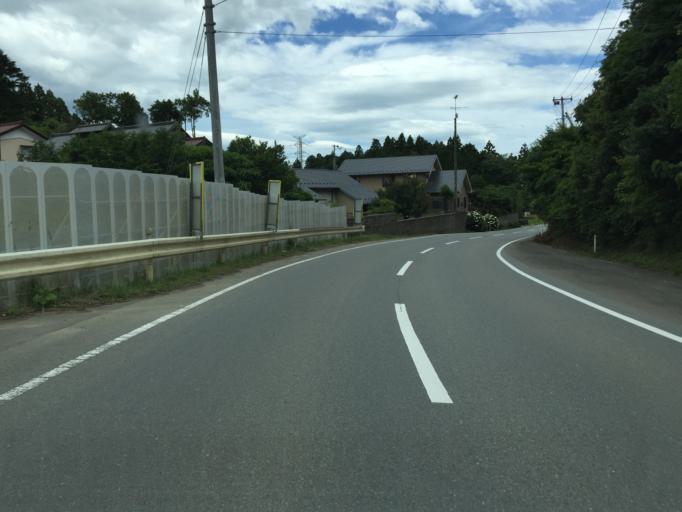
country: JP
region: Fukushima
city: Namie
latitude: 37.6497
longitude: 141.0155
